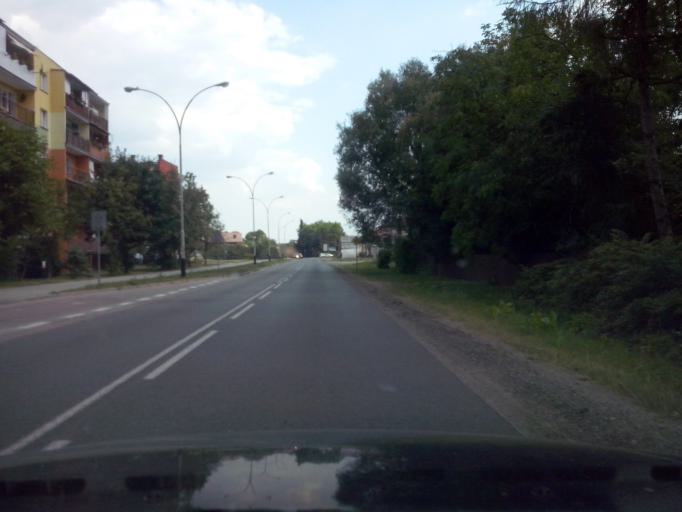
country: PL
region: Subcarpathian Voivodeship
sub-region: Powiat nizanski
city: Nisko
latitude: 50.5197
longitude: 22.1330
